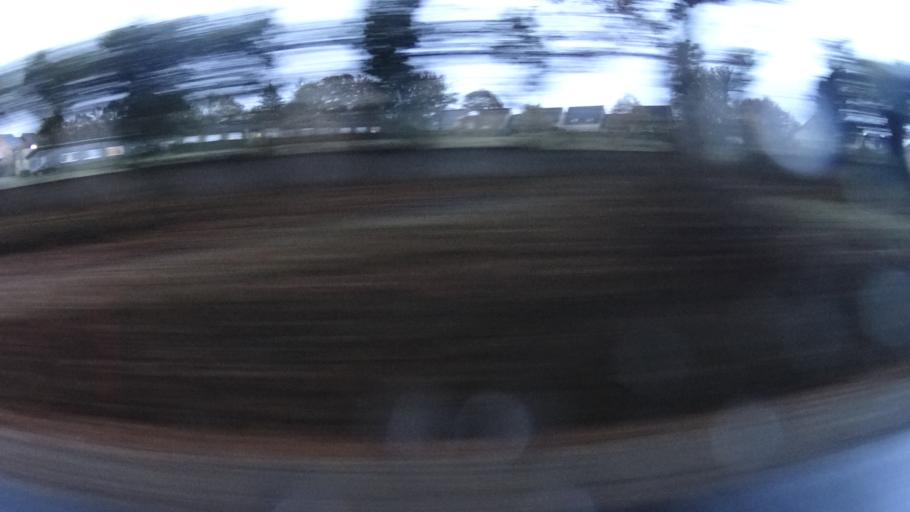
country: FR
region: Pays de la Loire
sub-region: Departement de la Loire-Atlantique
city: Saint-Nicolas-de-Redon
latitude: 47.6607
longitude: -2.0669
